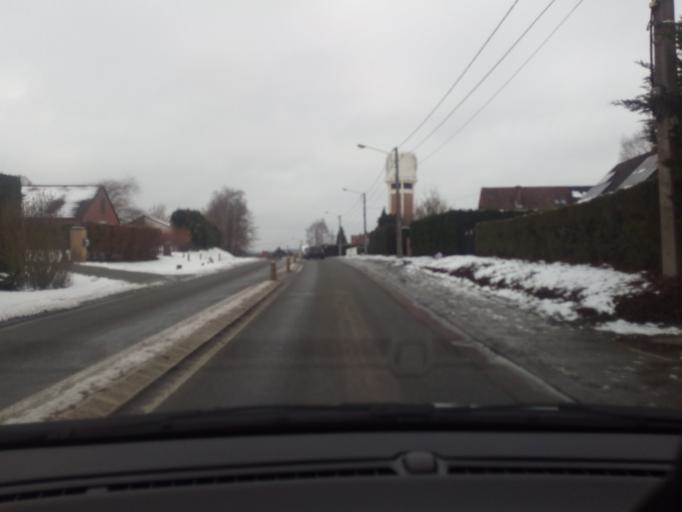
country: BE
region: Wallonia
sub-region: Province du Hainaut
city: Frameries
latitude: 50.4018
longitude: 3.9269
